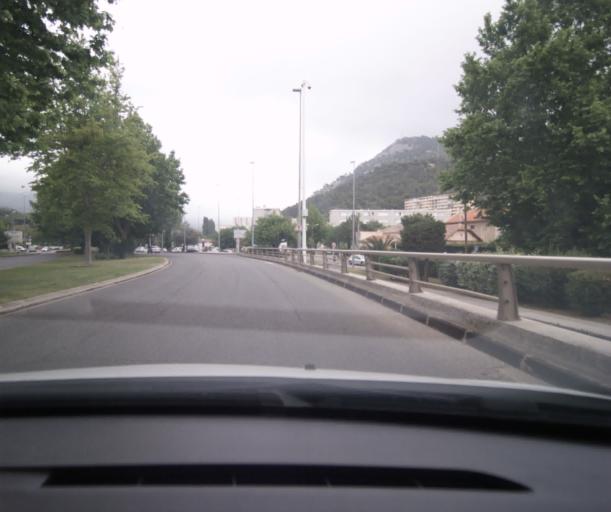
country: FR
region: Provence-Alpes-Cote d'Azur
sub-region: Departement du Var
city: Toulon
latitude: 43.1405
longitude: 5.9105
